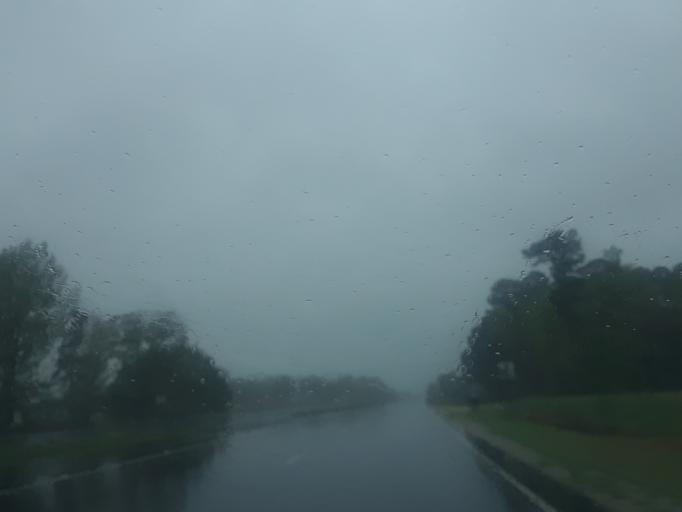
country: US
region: North Carolina
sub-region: Harnett County
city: Erwin
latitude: 35.3614
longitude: -78.7004
